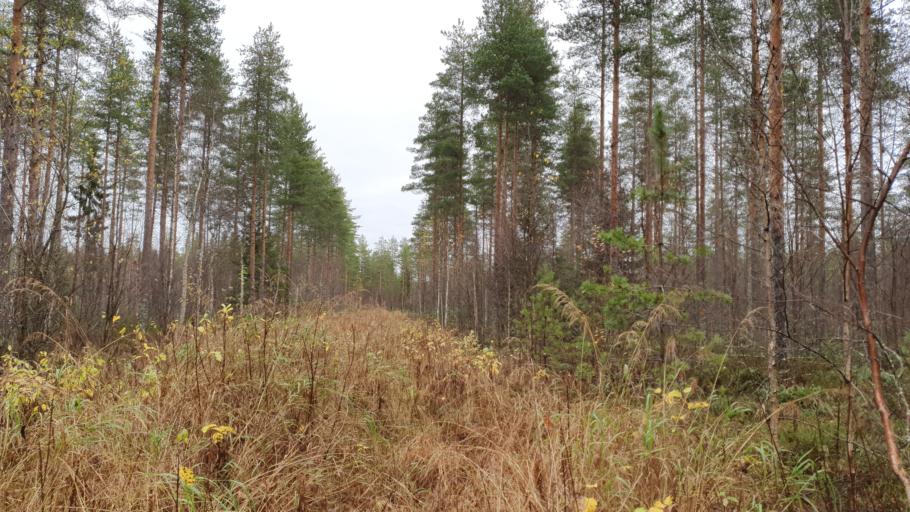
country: FI
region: Kainuu
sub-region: Kehys-Kainuu
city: Kuhmo
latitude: 64.1417
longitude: 29.4186
